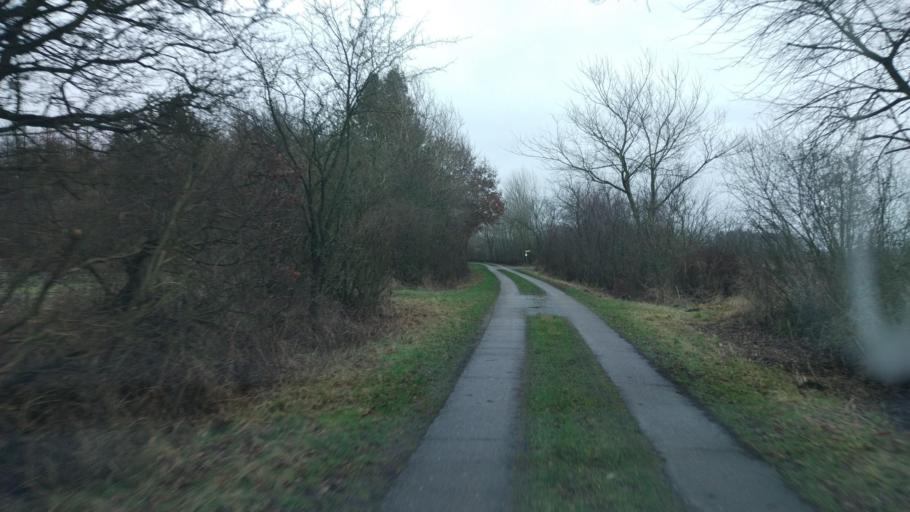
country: DE
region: Schleswig-Holstein
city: Gross Rheide
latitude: 54.4638
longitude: 9.4281
